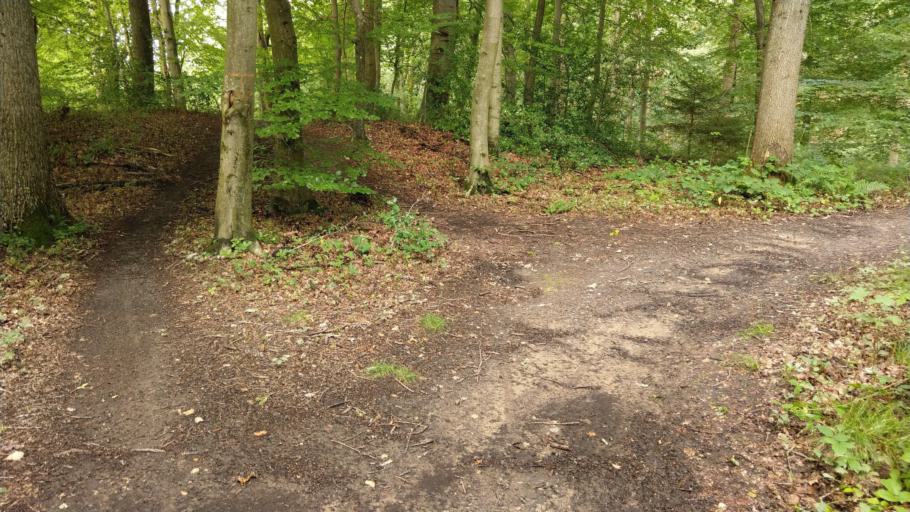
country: DE
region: North Rhine-Westphalia
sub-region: Regierungsbezirk Koln
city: Aachen
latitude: 50.7444
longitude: 6.0665
